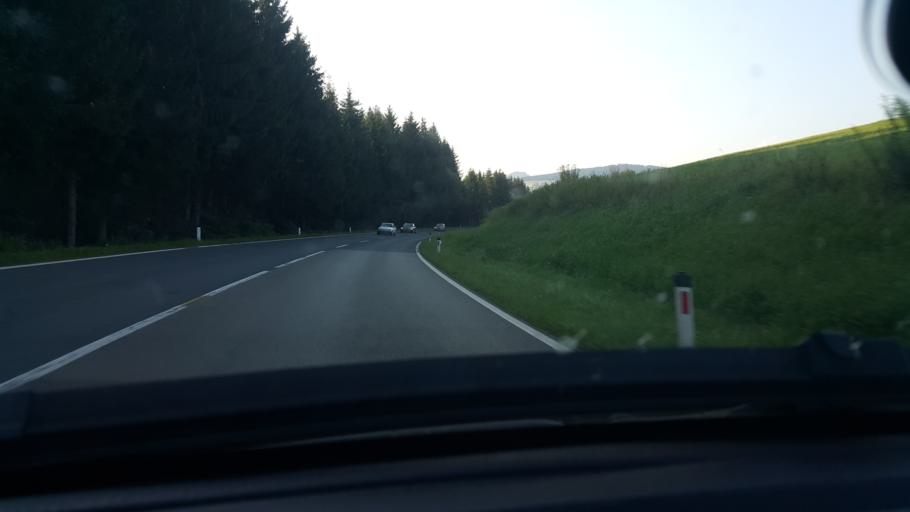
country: AT
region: Carinthia
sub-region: Politischer Bezirk Feldkirchen
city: Feldkirchen in Karnten
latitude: 46.7011
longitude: 14.1196
